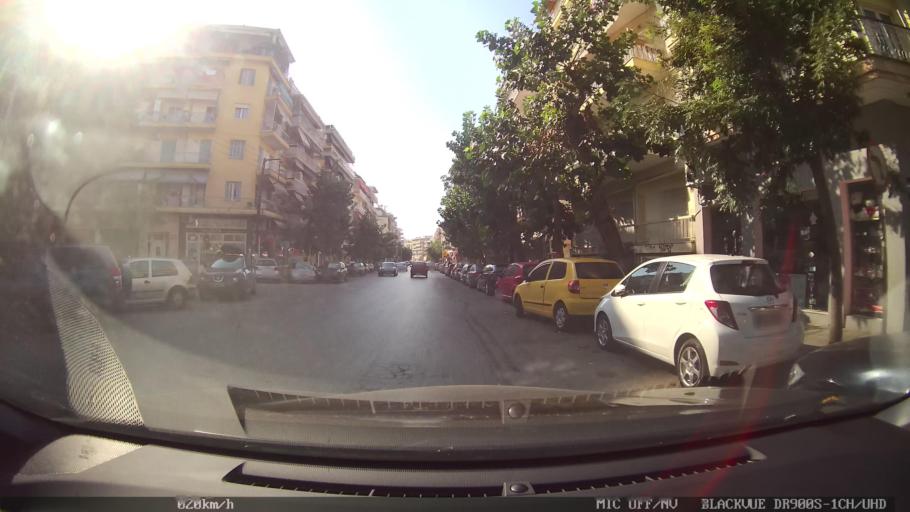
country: GR
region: Central Macedonia
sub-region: Nomos Thessalonikis
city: Triandria
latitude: 40.6152
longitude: 22.9580
